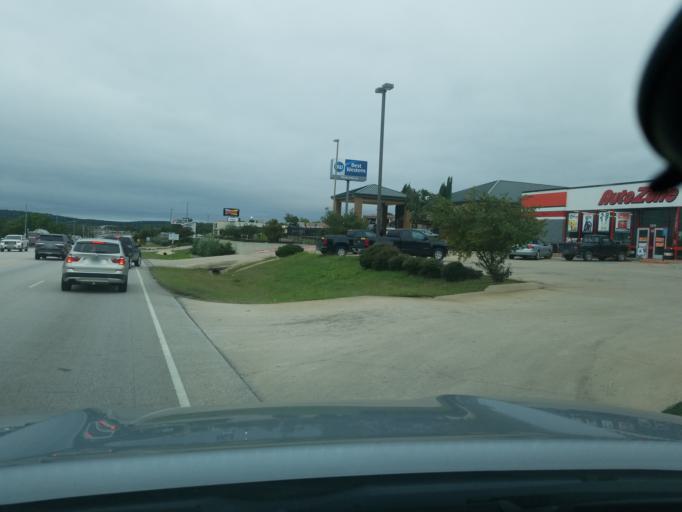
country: US
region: Texas
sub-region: Burnet County
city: Marble Falls
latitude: 30.5827
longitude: -98.2731
